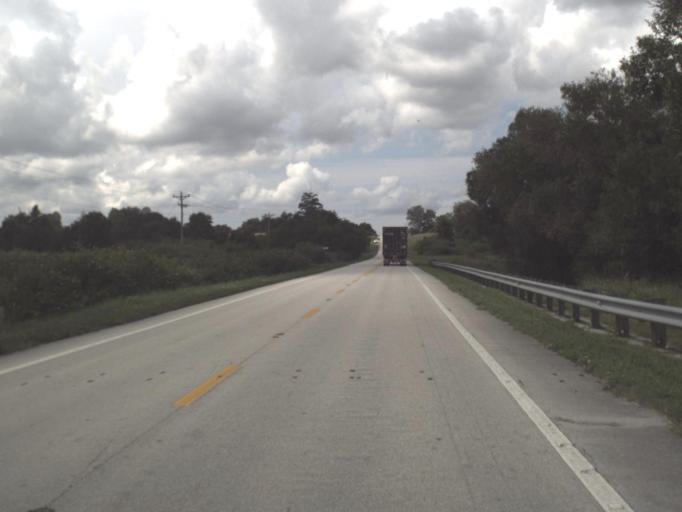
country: US
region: Florida
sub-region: Highlands County
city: Lake Placid
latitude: 27.2084
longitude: -81.2889
